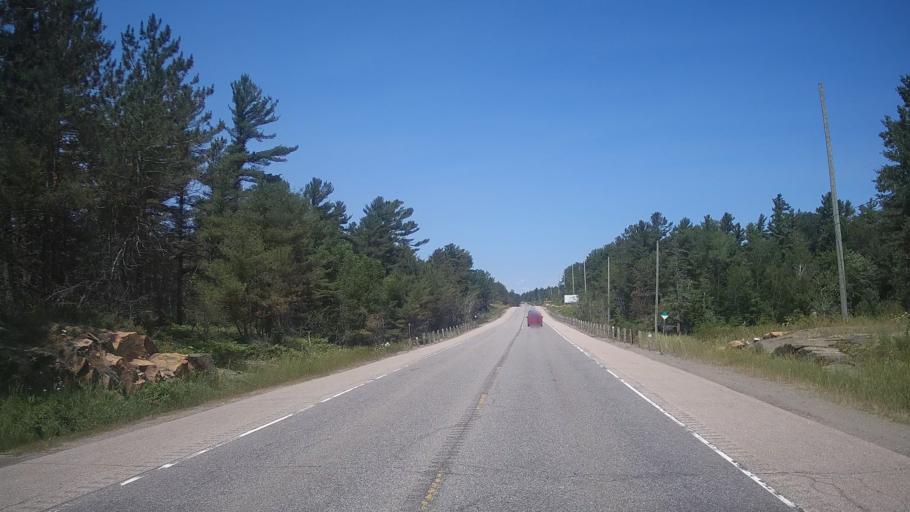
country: CA
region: Ontario
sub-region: Parry Sound District
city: Parry Sound
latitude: 45.6373
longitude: -80.3968
